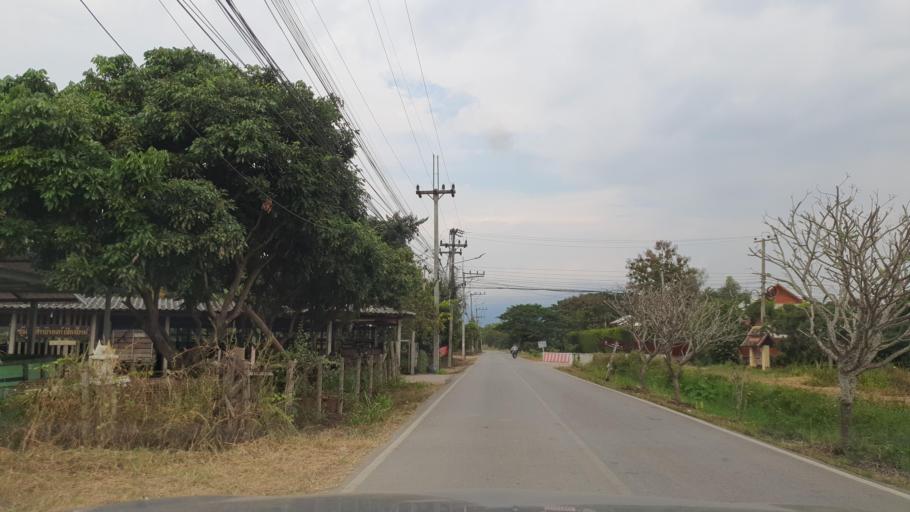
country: TH
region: Chiang Mai
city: Hang Dong
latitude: 18.6784
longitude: 98.9425
